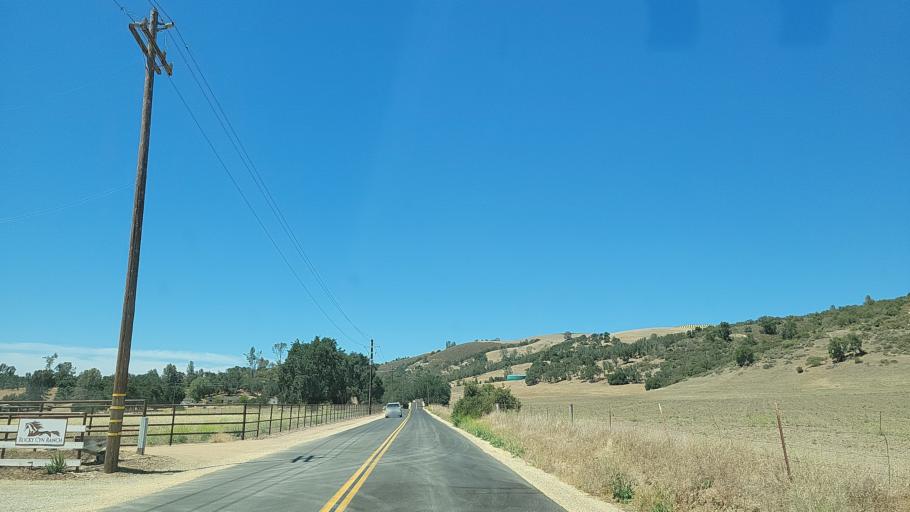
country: US
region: California
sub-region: San Luis Obispo County
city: Atascadero
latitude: 35.4700
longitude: -120.6235
